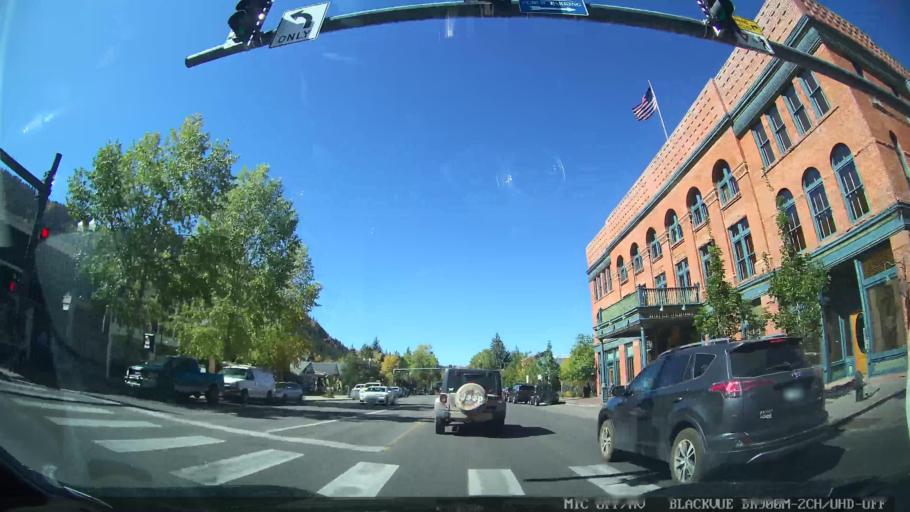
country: US
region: Colorado
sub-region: Pitkin County
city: Aspen
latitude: 39.1907
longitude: -106.8193
